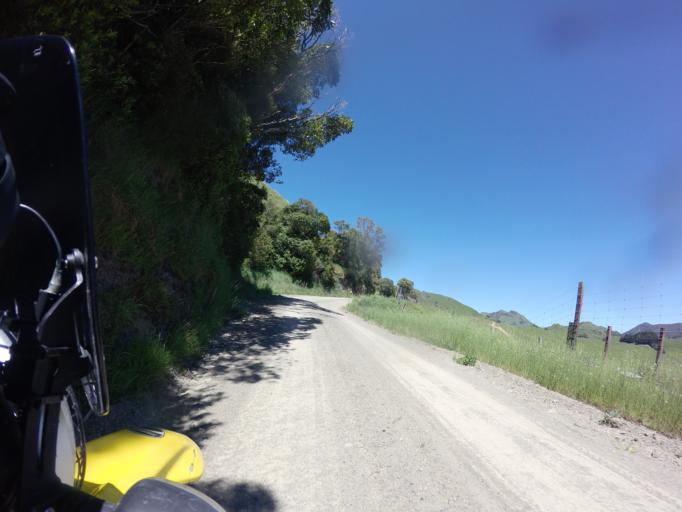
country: NZ
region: Bay of Plenty
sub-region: Opotiki District
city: Opotiki
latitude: -38.3999
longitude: 177.4576
